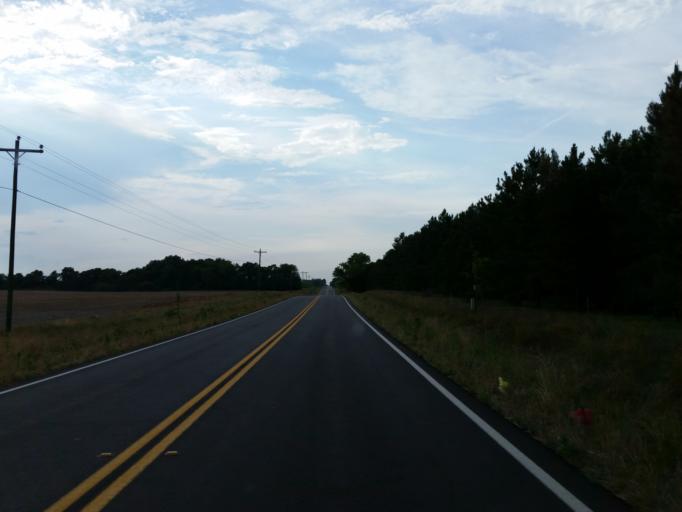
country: US
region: Georgia
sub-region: Dooly County
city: Unadilla
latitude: 32.2843
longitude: -83.7470
